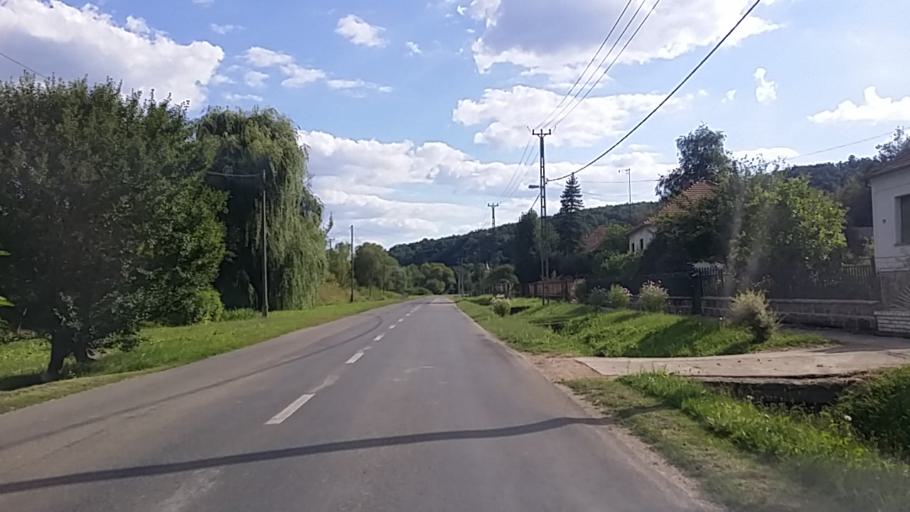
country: HU
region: Baranya
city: Sasd
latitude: 46.2038
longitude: 18.0836
